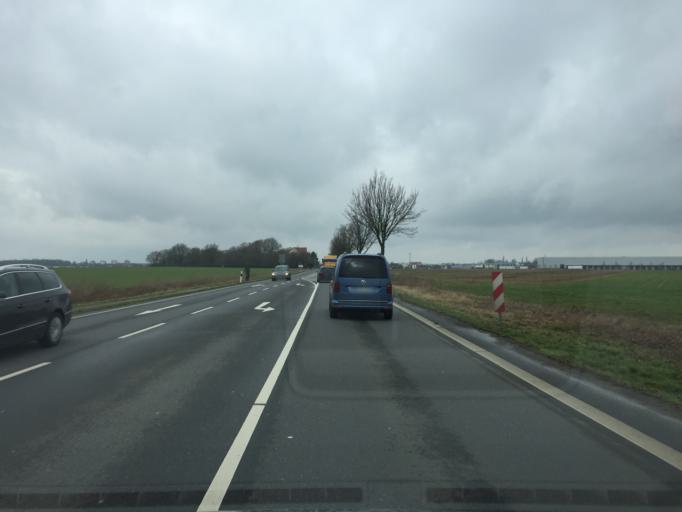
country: DE
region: Lower Saxony
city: Wunstorf
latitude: 52.4033
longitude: 9.4609
